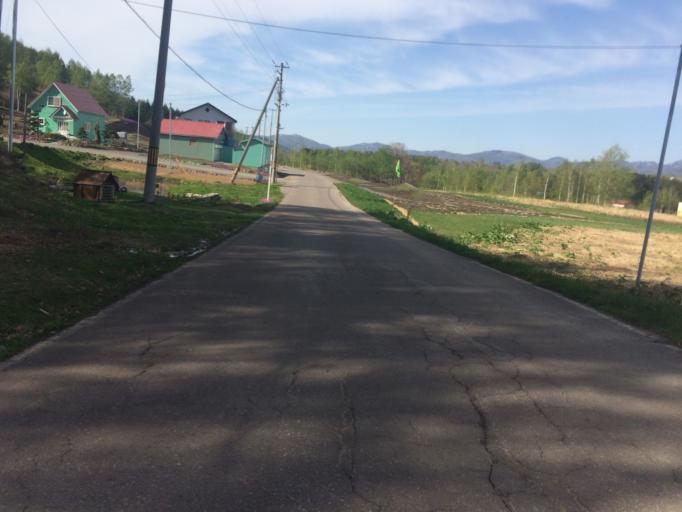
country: JP
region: Hokkaido
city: Niseko Town
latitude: 42.9073
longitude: 140.7402
